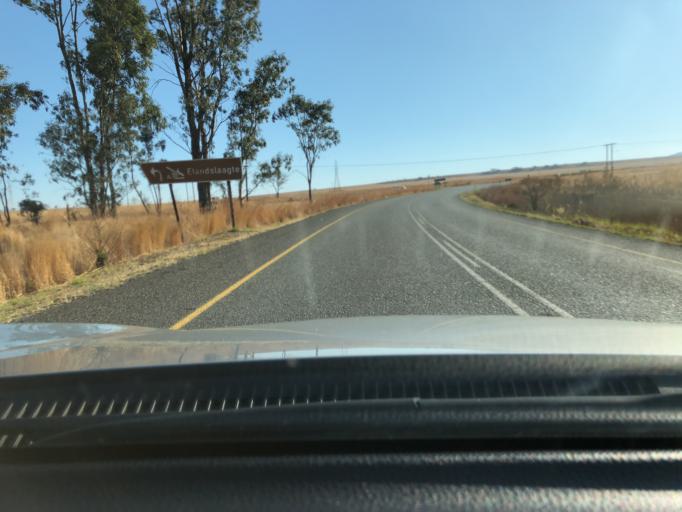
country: ZA
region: KwaZulu-Natal
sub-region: uThukela District Municipality
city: Ekuvukeni
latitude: -28.4064
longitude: 29.9556
